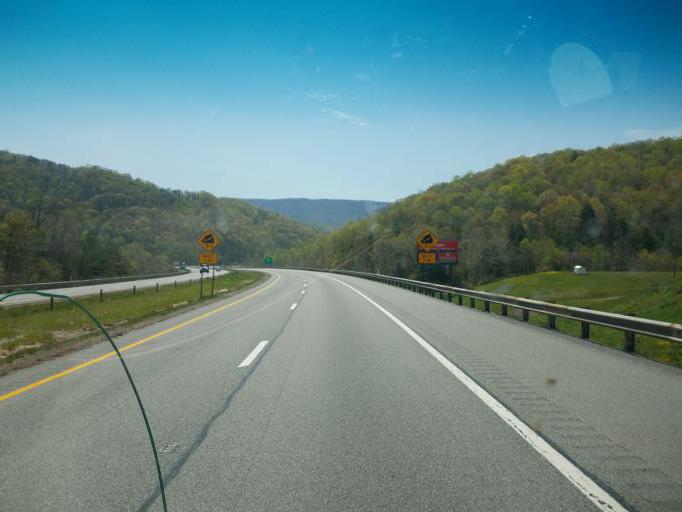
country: US
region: West Virginia
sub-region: Mercer County
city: Princeton
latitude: 37.3282
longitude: -81.0604
